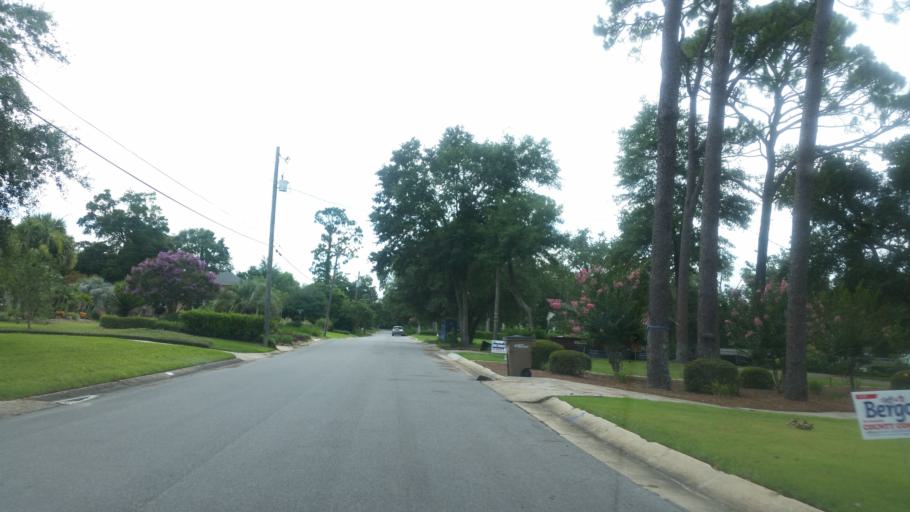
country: US
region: Florida
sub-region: Escambia County
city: East Pensacola Heights
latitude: 30.4472
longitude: -87.1958
